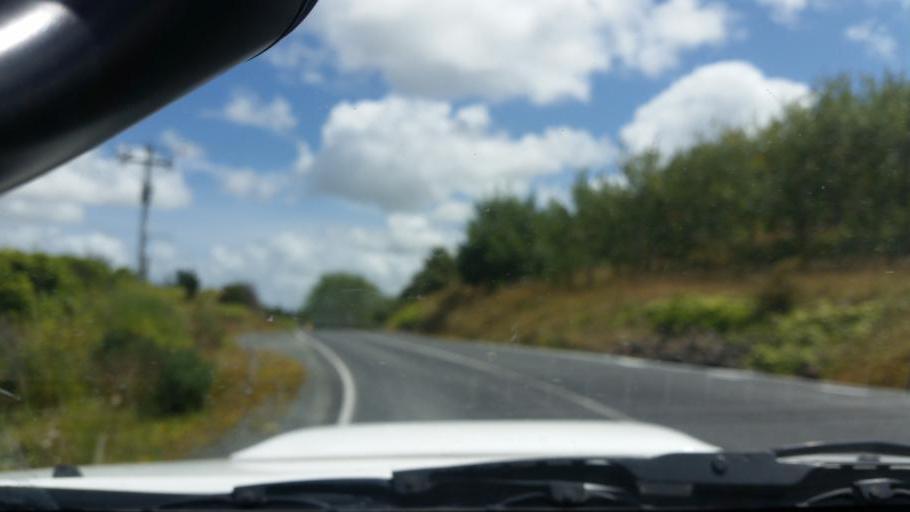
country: NZ
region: Northland
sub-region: Whangarei
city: Ruakaka
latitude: -36.0786
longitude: 174.2414
